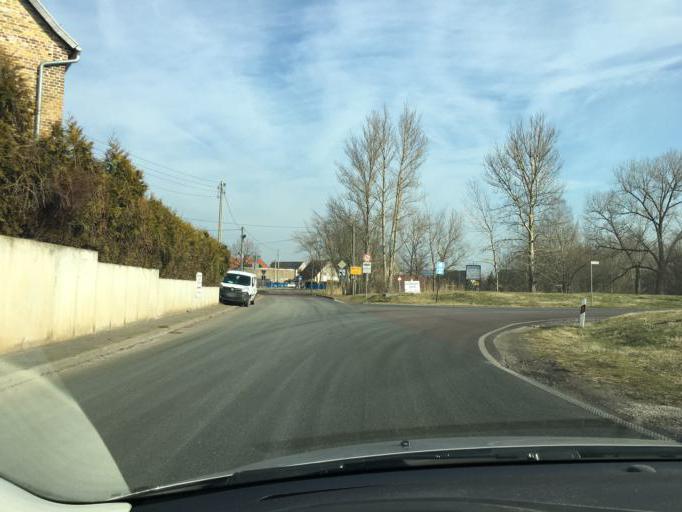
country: DE
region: Saxony-Anhalt
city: Grobers
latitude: 51.4362
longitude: 12.0974
